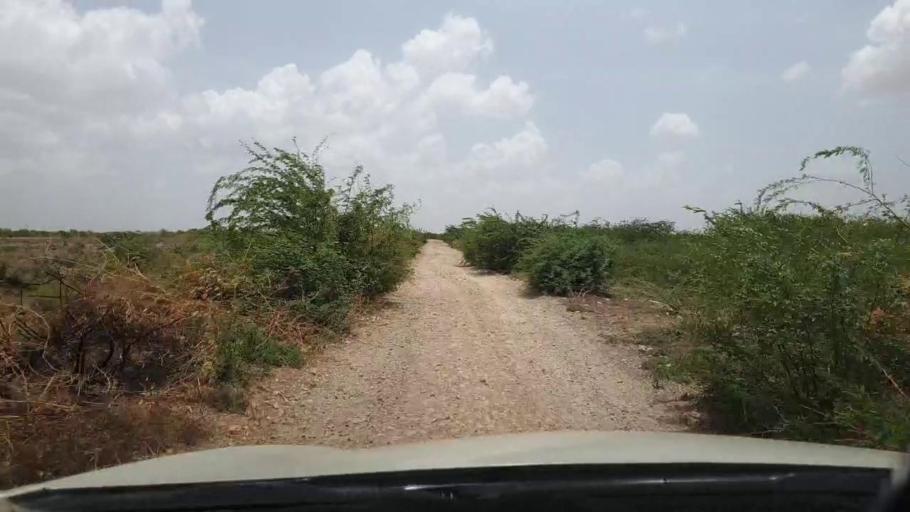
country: PK
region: Sindh
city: Kadhan
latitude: 24.3528
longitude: 68.9234
